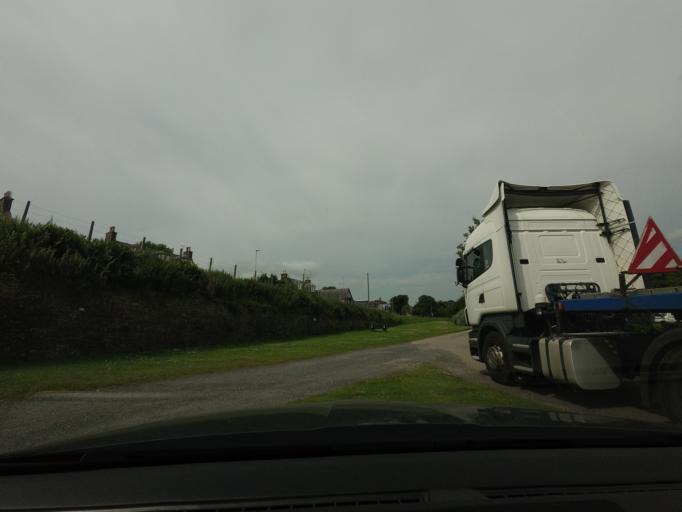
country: GB
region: Scotland
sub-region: Aberdeenshire
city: Turriff
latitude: 57.5329
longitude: -2.4592
